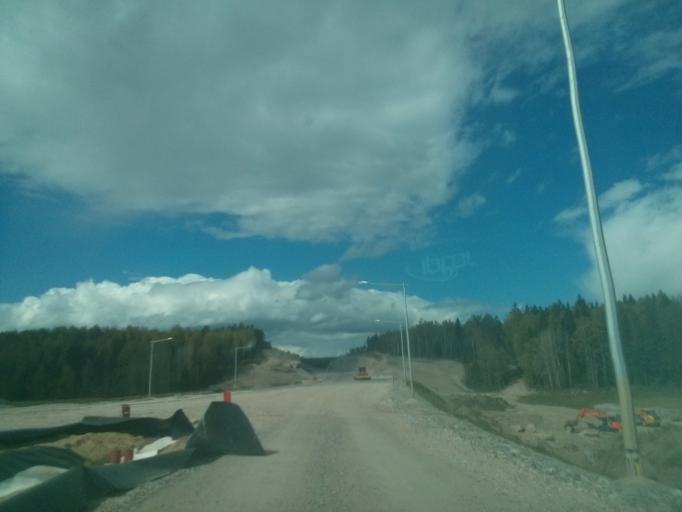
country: SE
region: Vaesternorrland
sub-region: Sundsvalls Kommun
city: Nolby
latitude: 62.2952
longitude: 17.3500
